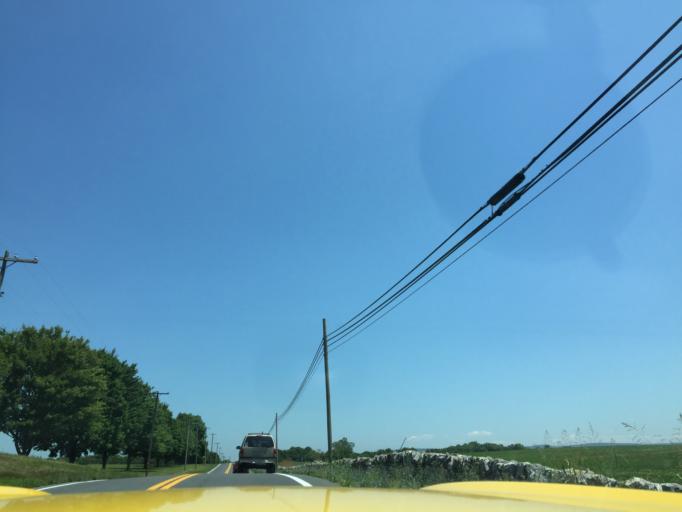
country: US
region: West Virginia
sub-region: Jefferson County
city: Charles Town
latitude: 39.2887
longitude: -77.8782
